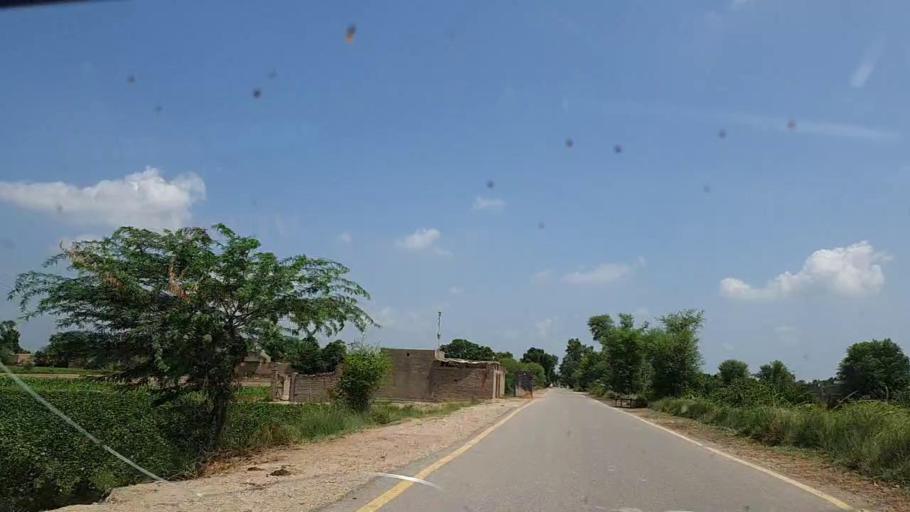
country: PK
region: Sindh
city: Tharu Shah
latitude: 26.9563
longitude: 68.1037
